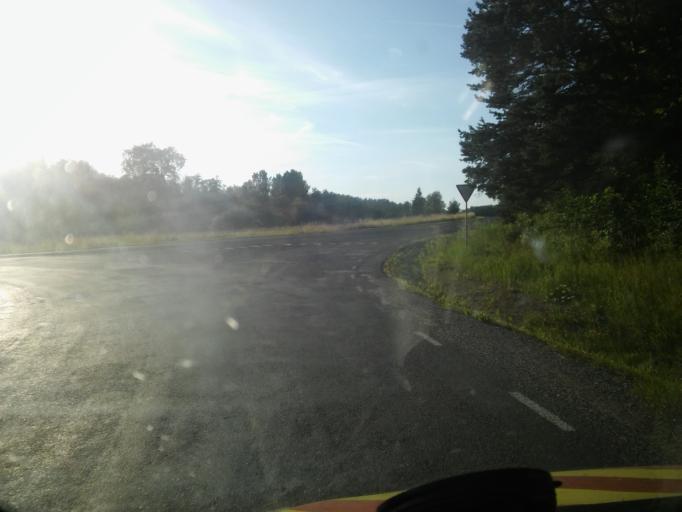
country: EE
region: Valgamaa
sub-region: Torva linn
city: Torva
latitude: 58.0212
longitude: 25.8807
